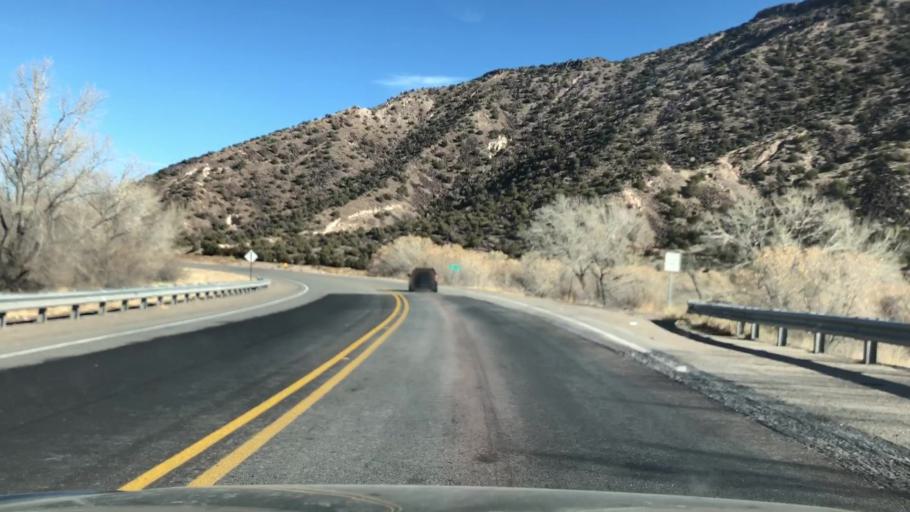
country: US
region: New Mexico
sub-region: Rio Arriba County
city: Ohkay Owingeh
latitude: 36.0948
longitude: -106.1312
